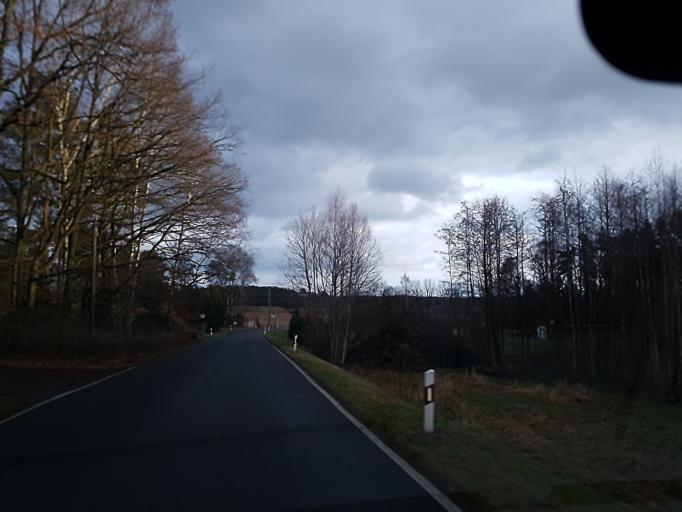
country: DE
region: Brandenburg
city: Elsterwerda
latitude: 51.4899
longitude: 13.5222
